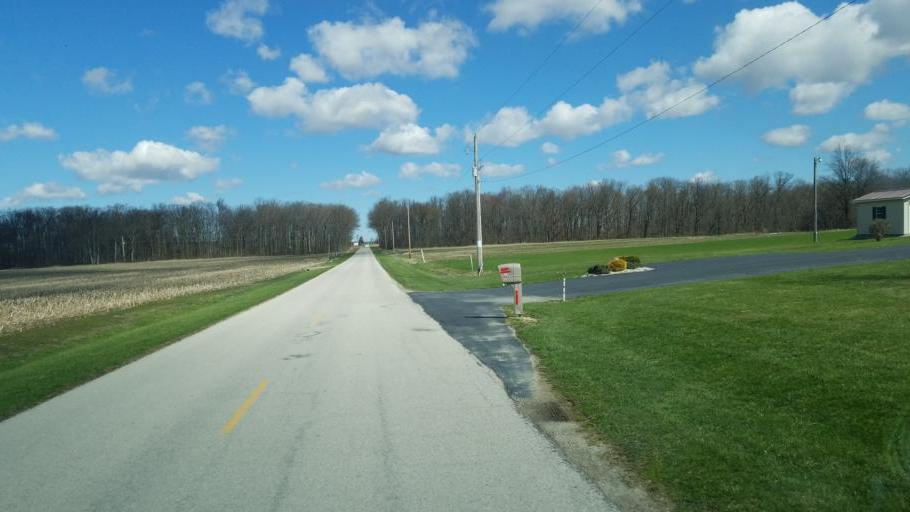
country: US
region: Ohio
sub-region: Sandusky County
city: Mount Carmel
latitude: 41.1805
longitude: -82.9379
